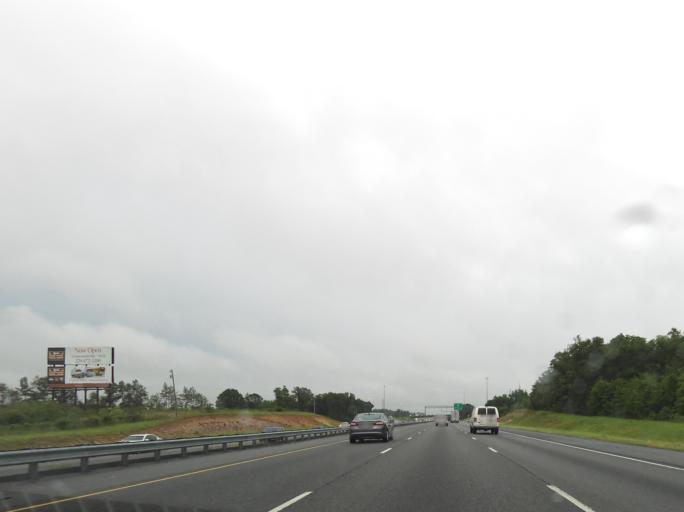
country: US
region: Georgia
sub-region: Crisp County
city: Cordele
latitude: 31.9131
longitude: -83.7404
